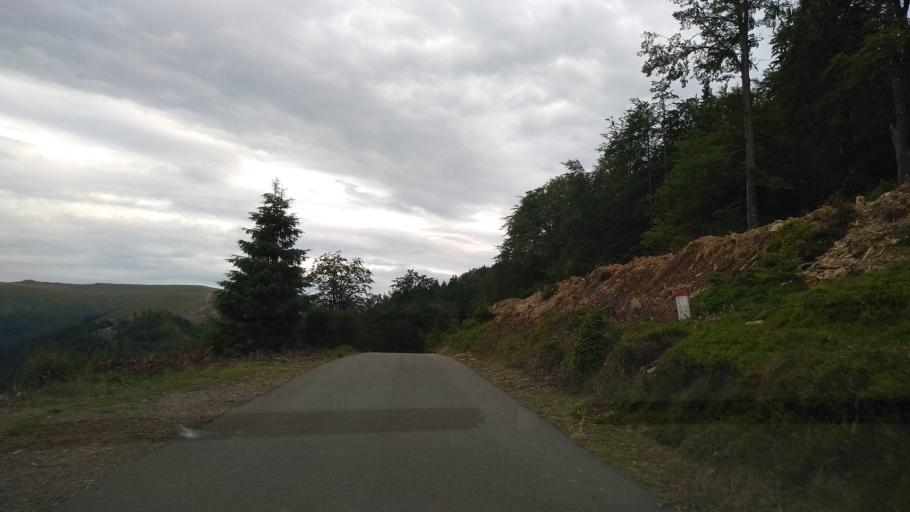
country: RO
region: Hunedoara
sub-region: Municipiul  Vulcan
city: Jiu-Paroseni
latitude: 45.3254
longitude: 23.2911
